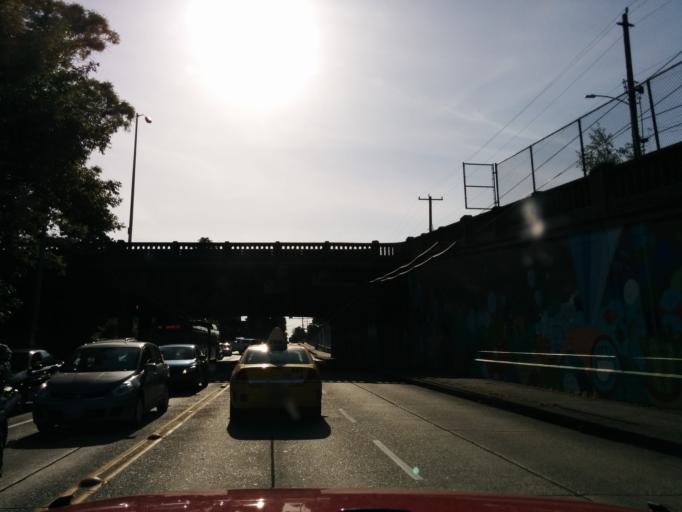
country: US
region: Washington
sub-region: King County
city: Seattle
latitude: 47.6620
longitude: -122.3467
